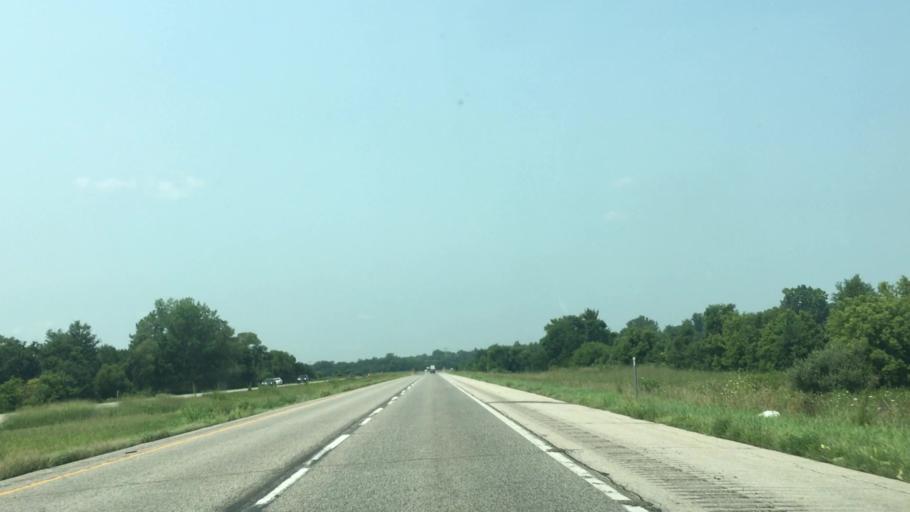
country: US
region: Iowa
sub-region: Linn County
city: Center Point
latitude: 42.1939
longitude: -91.8168
